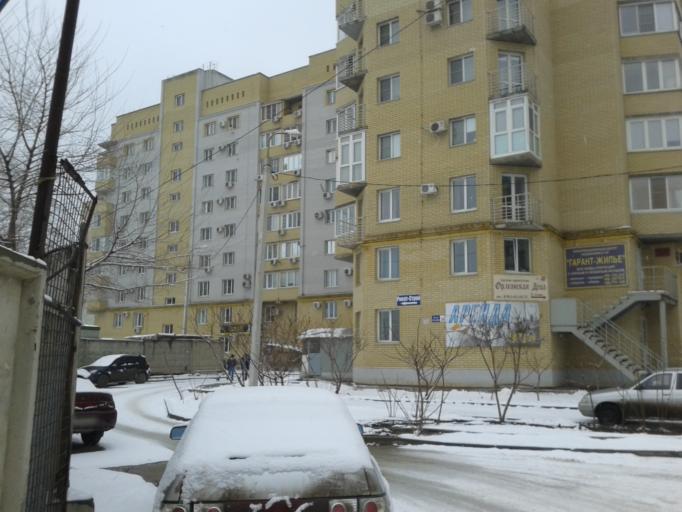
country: RU
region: Volgograd
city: Krasnoslobodsk
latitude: 48.5257
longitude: 44.5614
